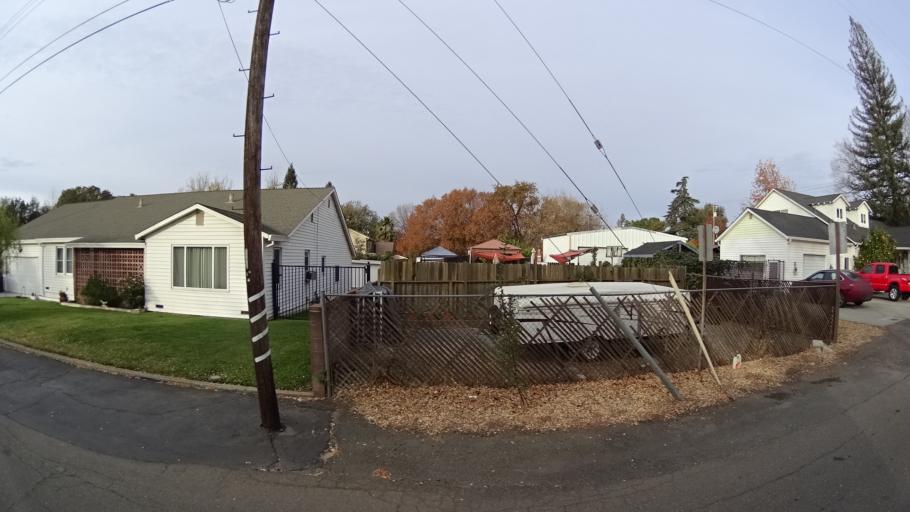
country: US
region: California
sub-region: Sacramento County
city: Citrus Heights
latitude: 38.7181
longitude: -121.2766
